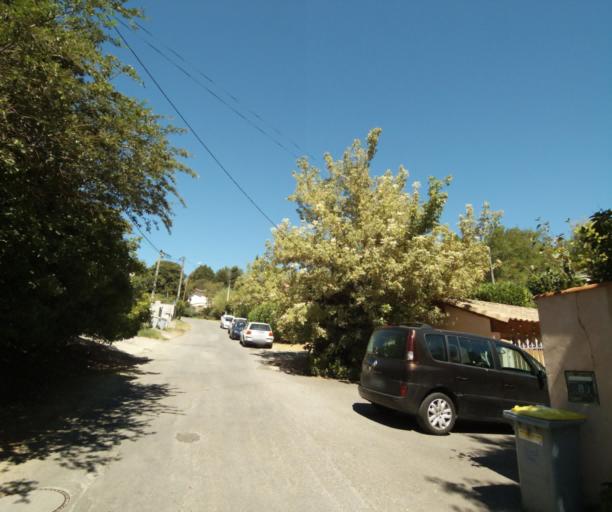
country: FR
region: Midi-Pyrenees
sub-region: Departement de la Haute-Garonne
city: Auzeville-Tolosane
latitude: 43.5164
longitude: 1.4846
